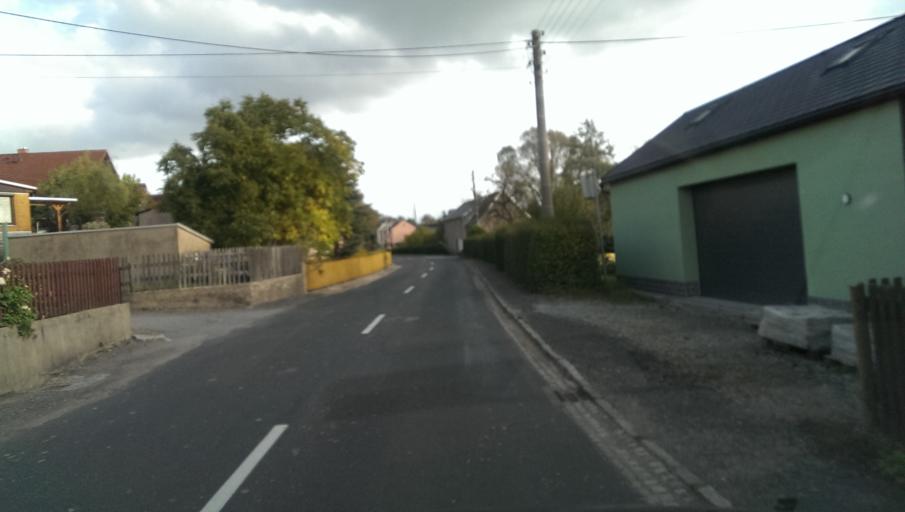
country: DE
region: Saxony
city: Haselbachtal
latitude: 51.2347
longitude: 14.0446
